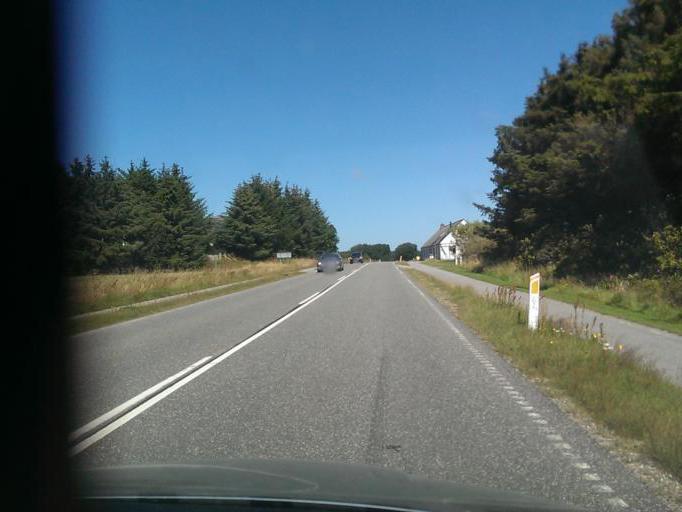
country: DK
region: North Denmark
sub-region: Jammerbugt Kommune
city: Pandrup
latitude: 57.3038
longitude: 9.6992
